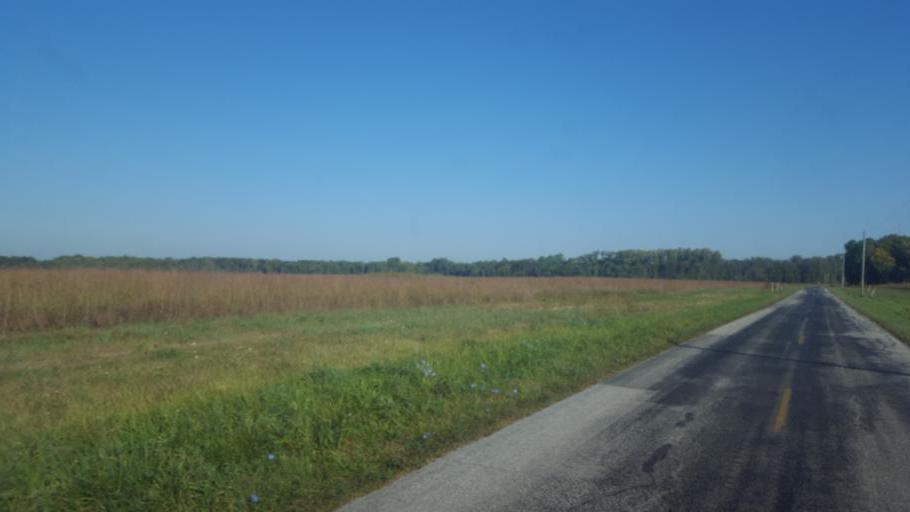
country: US
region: Ohio
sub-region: Union County
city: Richwood
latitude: 40.5563
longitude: -83.3185
